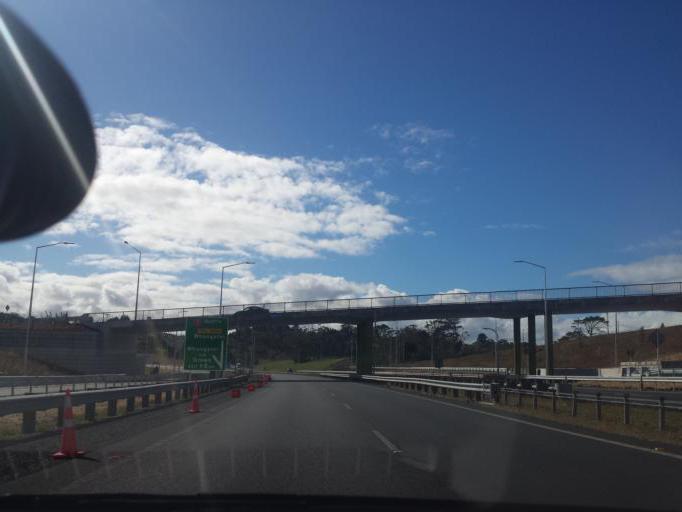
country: NZ
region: Auckland
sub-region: Auckland
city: Rothesay Bay
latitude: -36.6041
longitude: 174.6619
